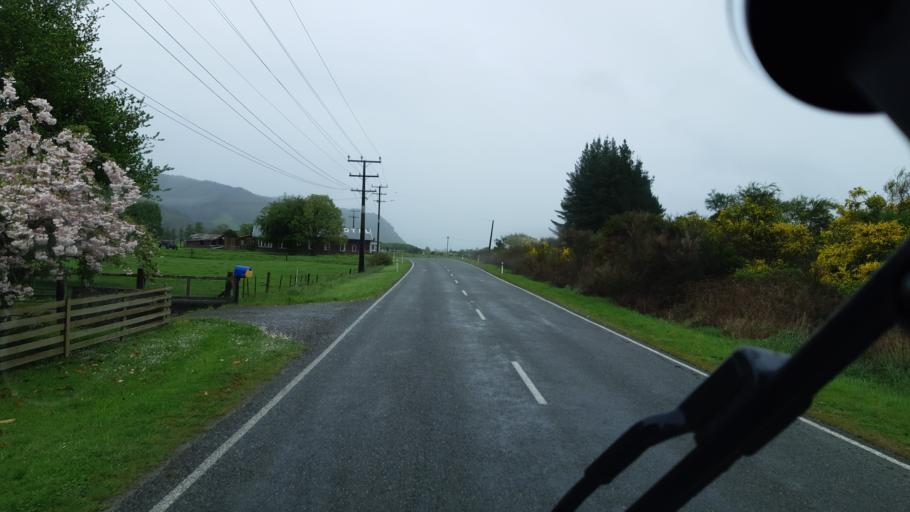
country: NZ
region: West Coast
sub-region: Buller District
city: Westport
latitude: -42.1898
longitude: 171.7219
